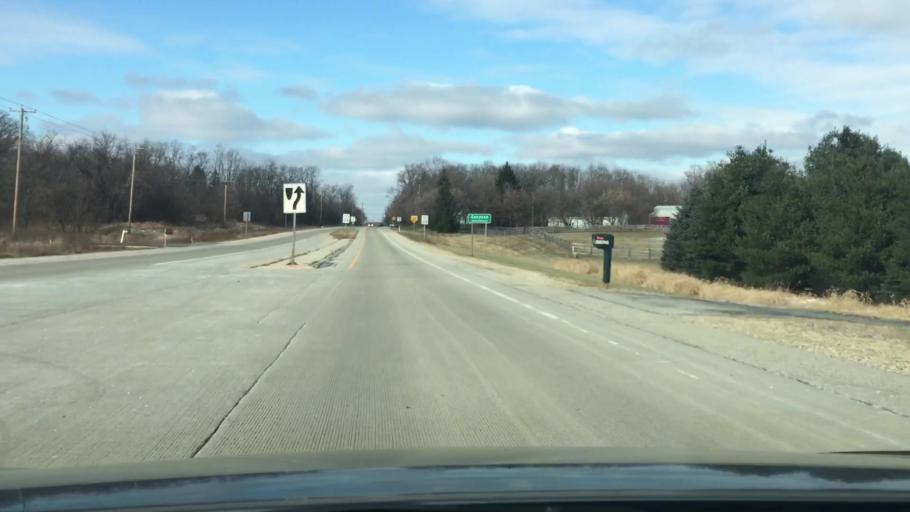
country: US
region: Wisconsin
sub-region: Waukesha County
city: North Prairie
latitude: 42.9492
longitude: -88.3533
